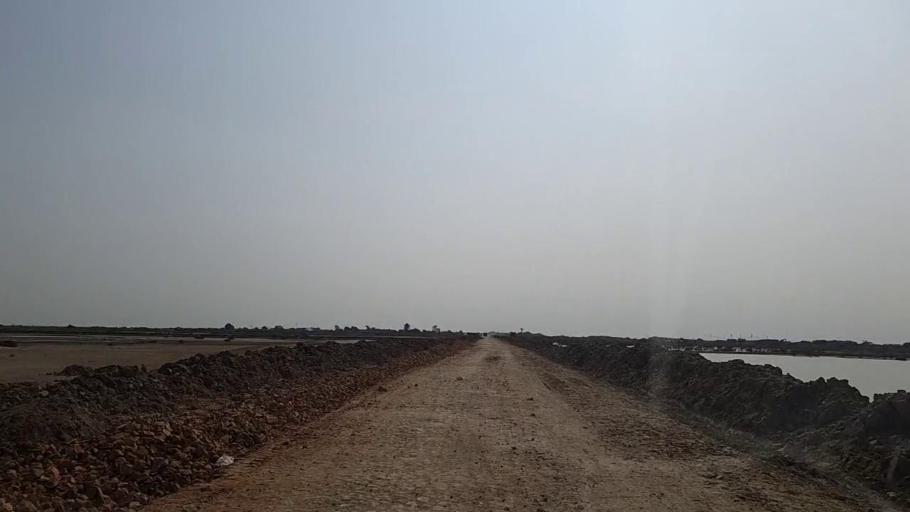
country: PK
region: Sindh
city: Chuhar Jamali
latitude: 24.1964
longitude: 67.8485
